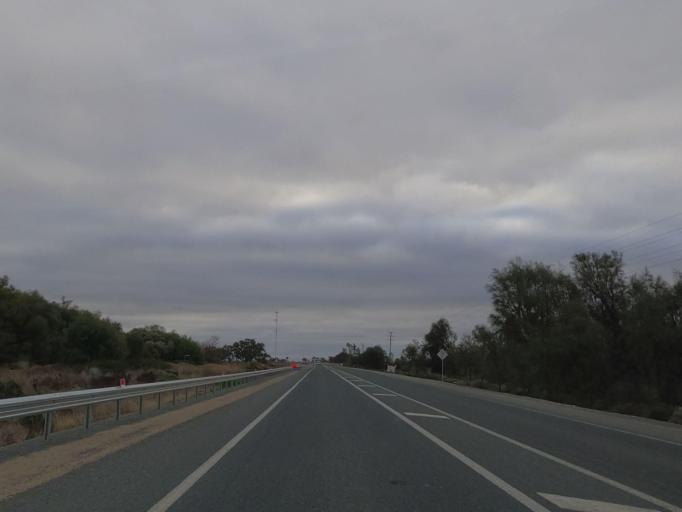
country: AU
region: Victoria
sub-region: Swan Hill
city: Swan Hill
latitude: -35.5351
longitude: 143.7445
